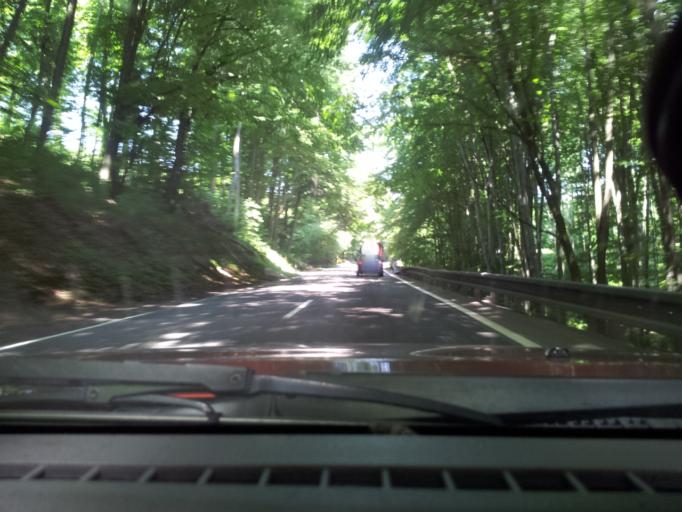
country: SK
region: Trnavsky
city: Smolenice
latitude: 48.5710
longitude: 17.4636
